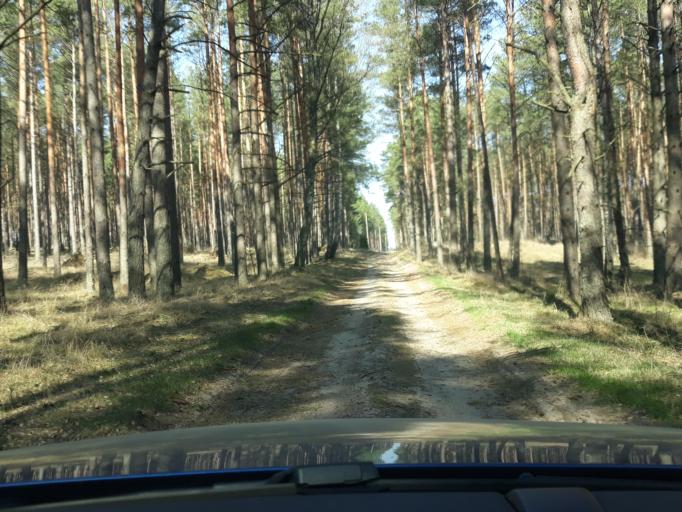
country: PL
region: Pomeranian Voivodeship
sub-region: Powiat bytowski
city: Lipnica
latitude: 53.8652
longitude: 17.4296
